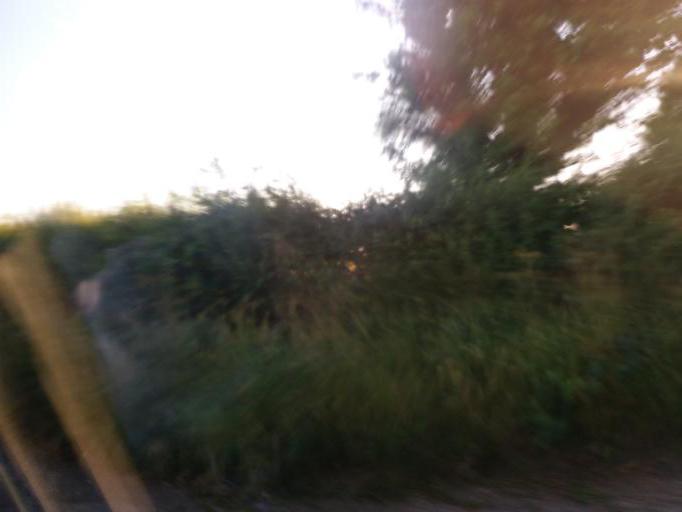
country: IE
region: Leinster
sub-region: An Mhi
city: Ashbourne
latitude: 53.5437
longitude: -6.3615
